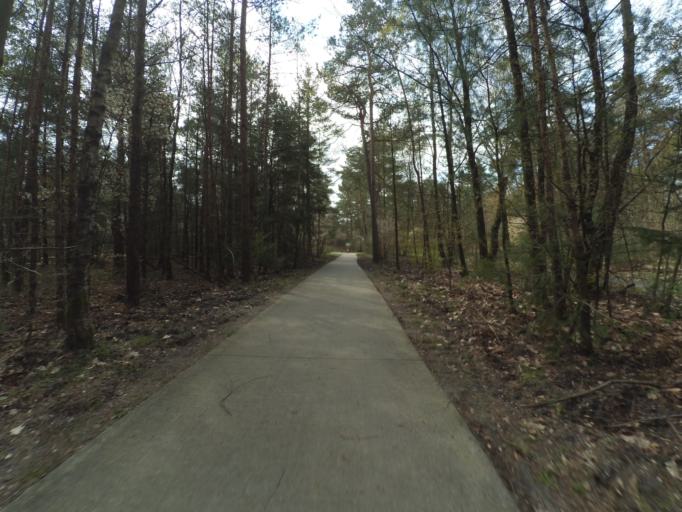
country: NL
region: Gelderland
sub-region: Gemeente Nunspeet
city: Nunspeet
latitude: 52.3698
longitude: 5.8237
